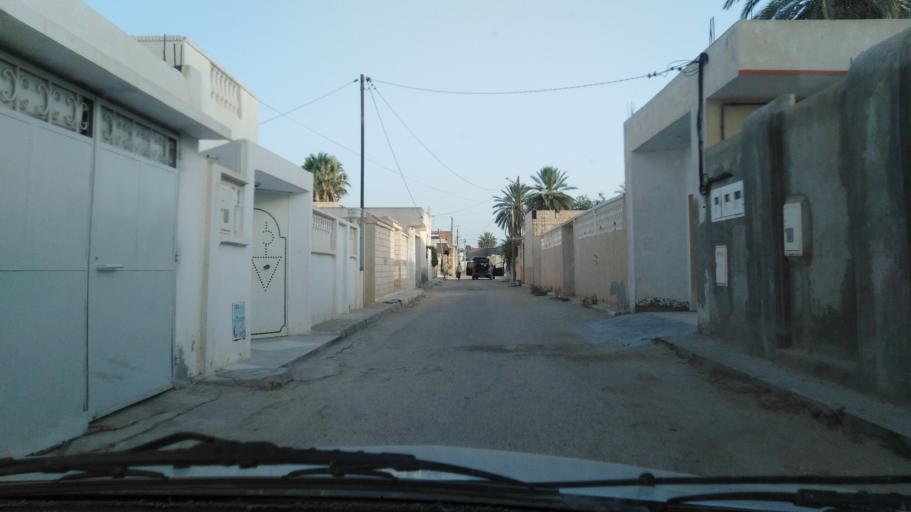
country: TN
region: Qabis
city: Gabes
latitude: 33.9573
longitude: 9.9968
